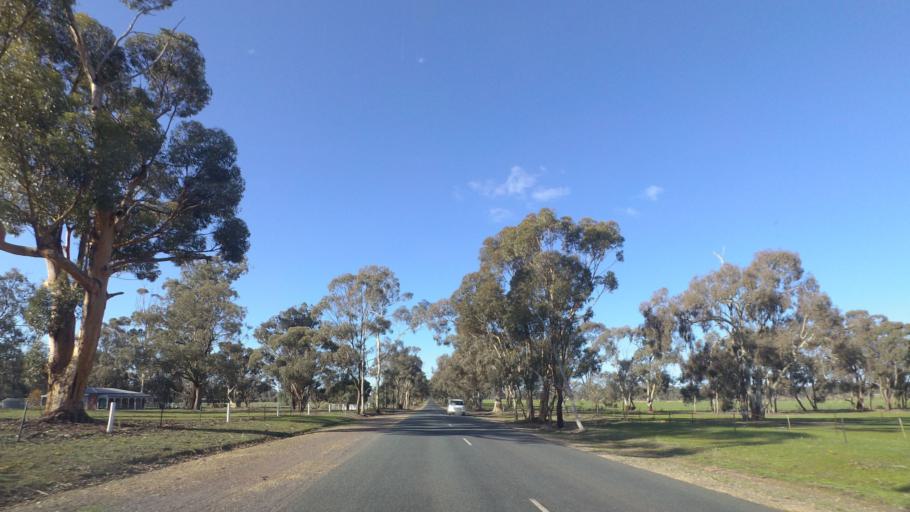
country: AU
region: Victoria
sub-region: Greater Bendigo
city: Epsom
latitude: -36.6619
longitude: 144.4555
